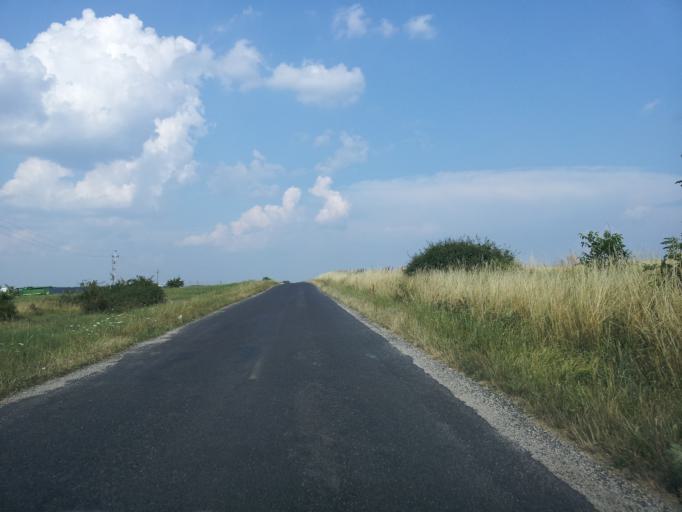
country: HU
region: Veszprem
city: Nemesvamos
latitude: 47.0109
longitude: 17.7962
